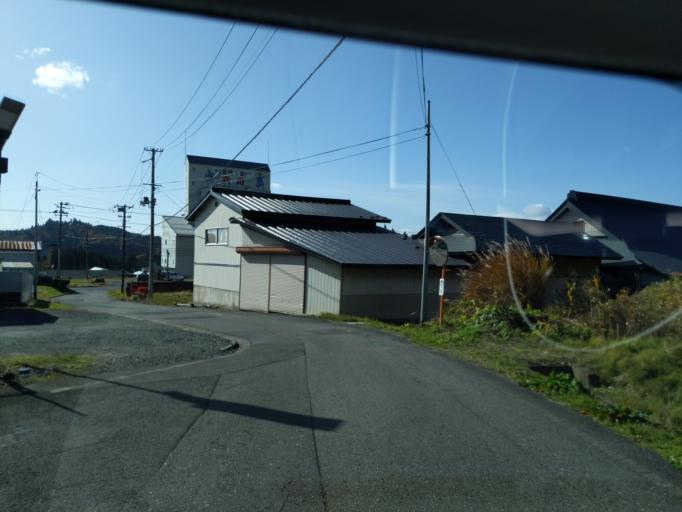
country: JP
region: Iwate
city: Ichinoseki
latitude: 39.0204
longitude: 141.0945
